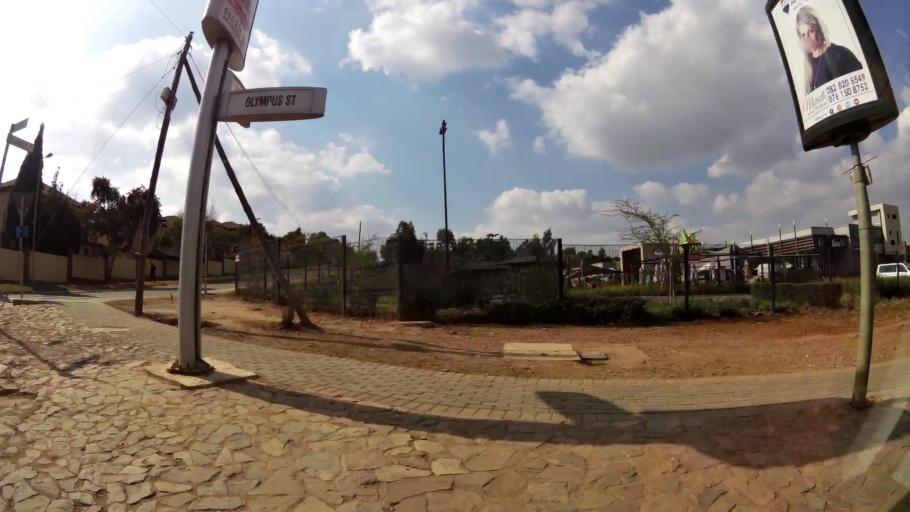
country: ZA
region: Gauteng
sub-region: City of Tshwane Metropolitan Municipality
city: Pretoria
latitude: -25.7983
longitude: 28.3319
